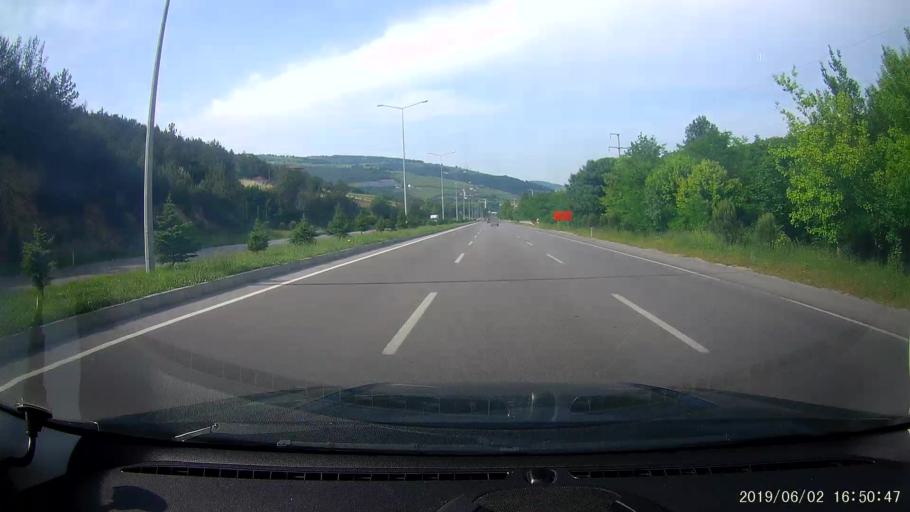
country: TR
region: Samsun
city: Taflan
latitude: 41.2621
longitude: 36.1756
